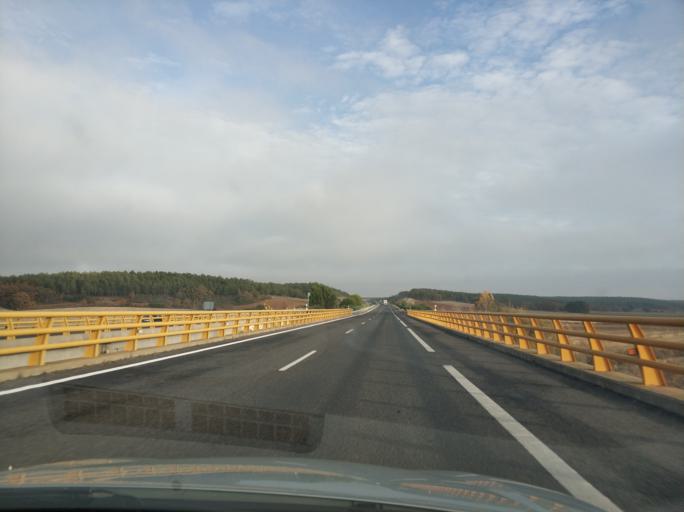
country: ES
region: Castille and Leon
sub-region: Provincia de Palencia
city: Ledigos
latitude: 42.3638
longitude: -4.8544
